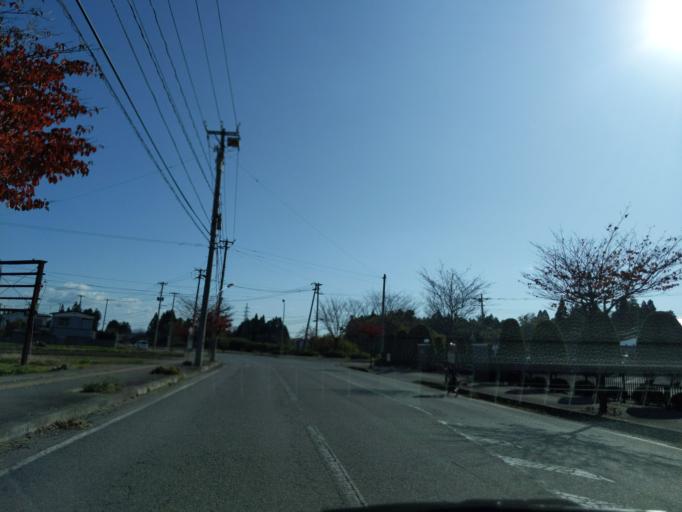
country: JP
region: Iwate
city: Ichinoseki
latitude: 38.9313
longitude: 141.0961
